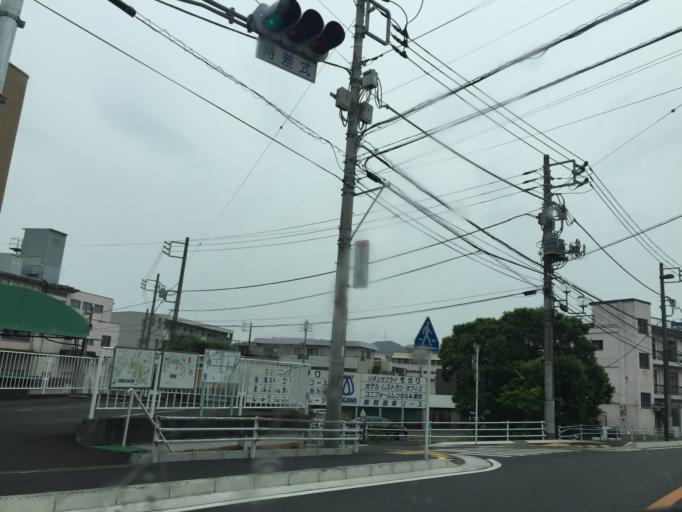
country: JP
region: Shizuoka
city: Ito
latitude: 34.9791
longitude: 138.9493
